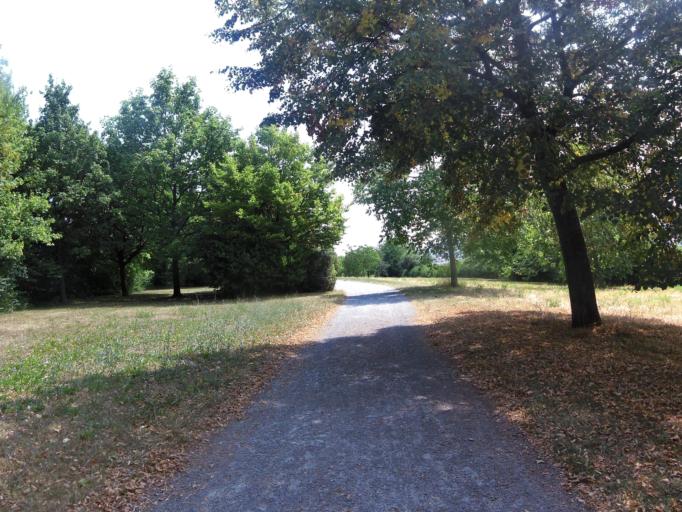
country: DE
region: Bavaria
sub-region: Regierungsbezirk Unterfranken
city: Wuerzburg
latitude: 49.8070
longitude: 9.9482
